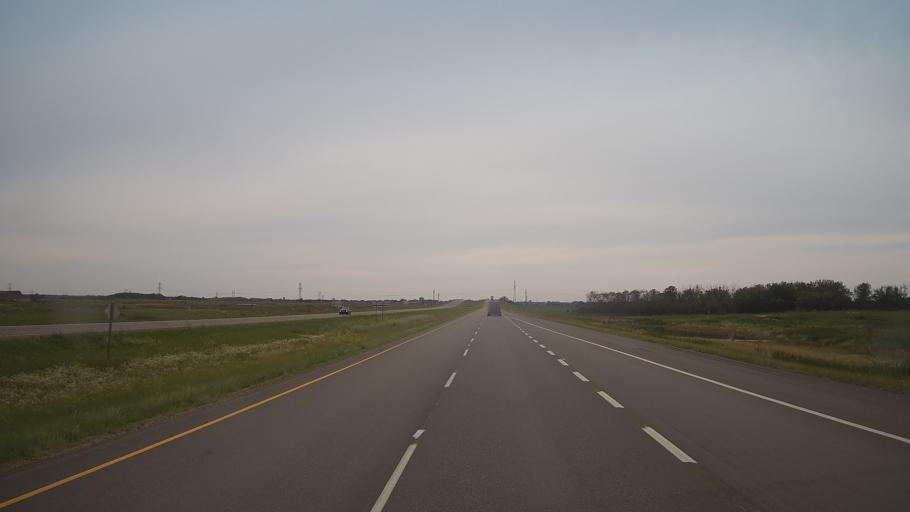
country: CA
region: Saskatchewan
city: Saskatoon
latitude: 52.0614
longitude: -106.6008
